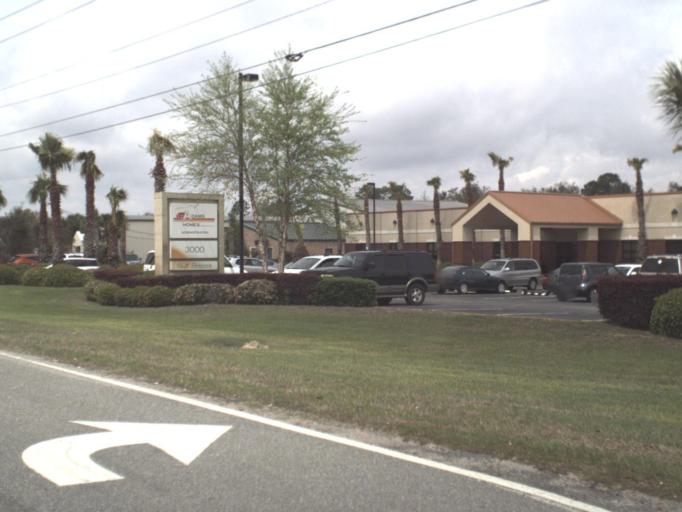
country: US
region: Florida
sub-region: Santa Rosa County
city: Oriole Beach
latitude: 30.3852
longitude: -87.0984
